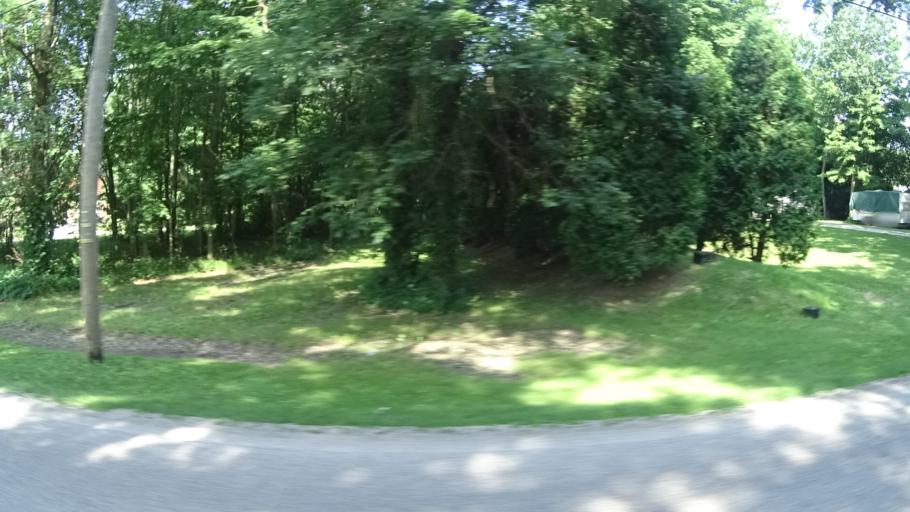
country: US
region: Ohio
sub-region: Lorain County
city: Vermilion
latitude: 41.3662
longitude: -82.4177
